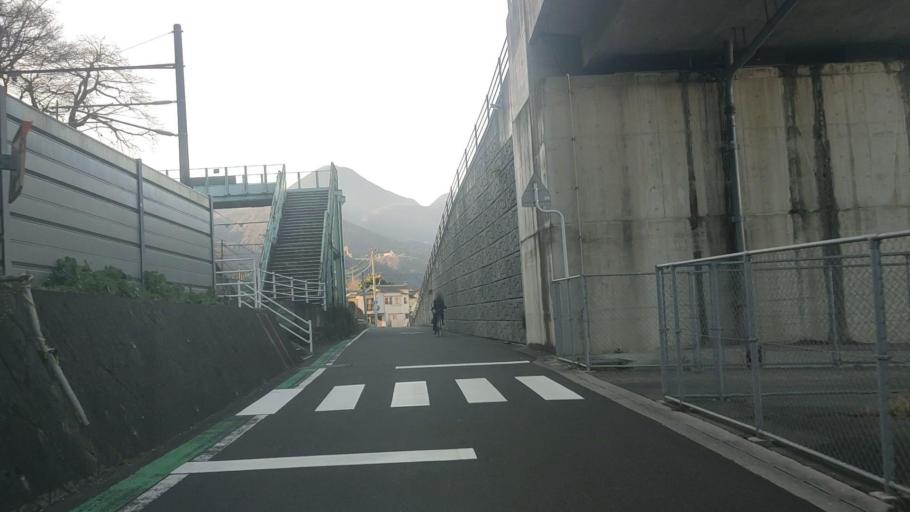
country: JP
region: Oita
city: Beppu
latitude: 33.2684
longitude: 131.5090
